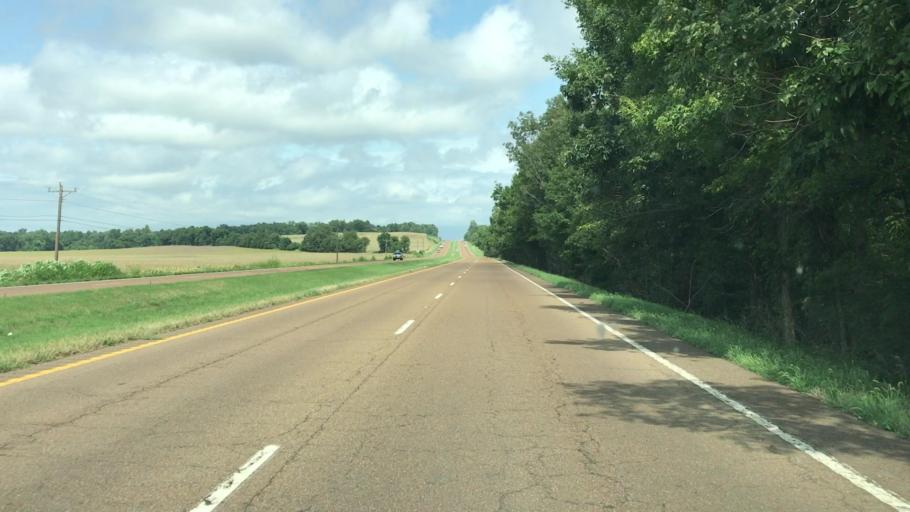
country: US
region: Tennessee
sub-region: Obion County
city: Englewood
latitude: 36.3642
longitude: -89.1296
